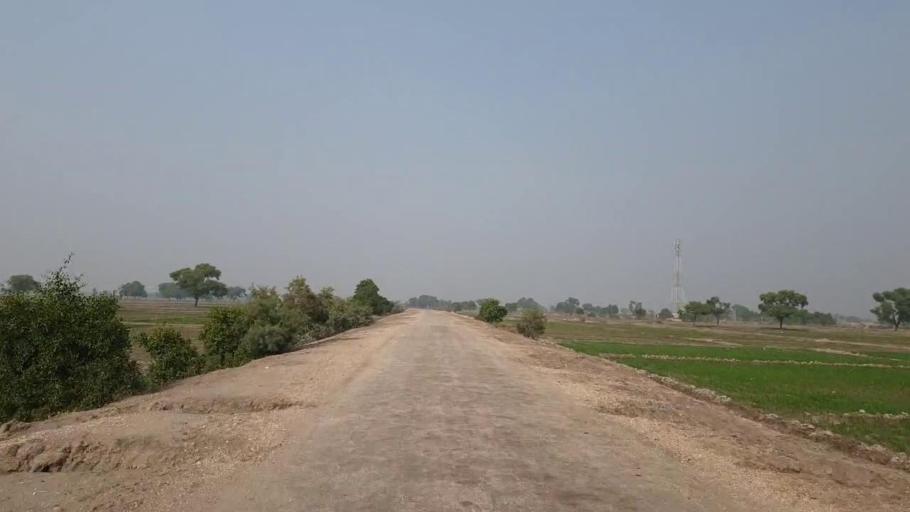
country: PK
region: Sindh
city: Bhan
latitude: 26.4948
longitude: 67.6988
